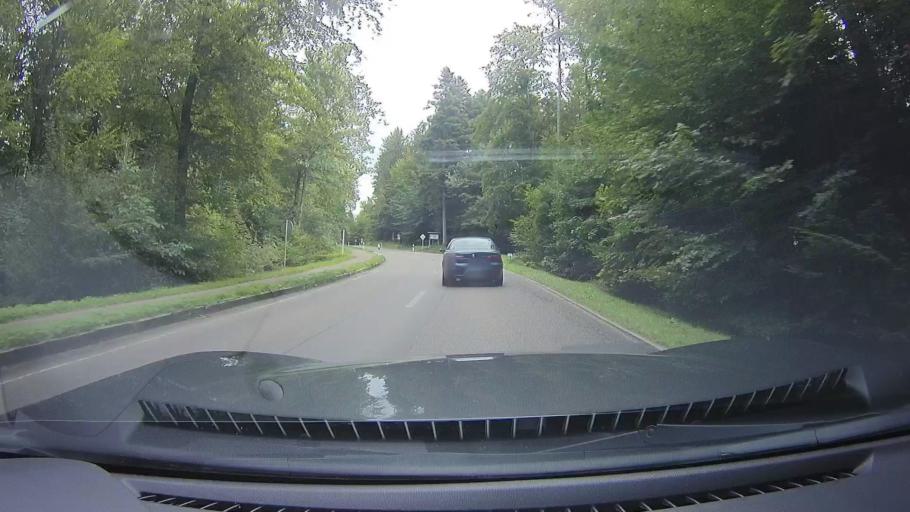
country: DE
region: Baden-Wuerttemberg
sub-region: Regierungsbezirk Stuttgart
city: Althutte
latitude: 48.9231
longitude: 9.5874
